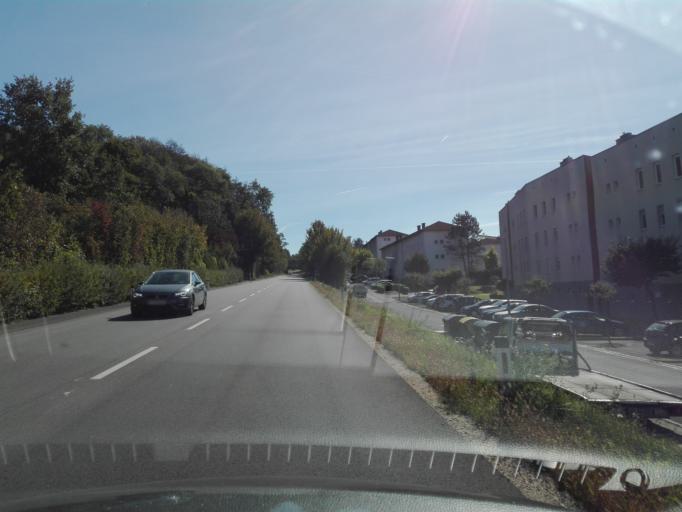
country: AT
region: Upper Austria
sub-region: Politischer Bezirk Linz-Land
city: Ansfelden
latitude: 48.2395
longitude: 14.3356
